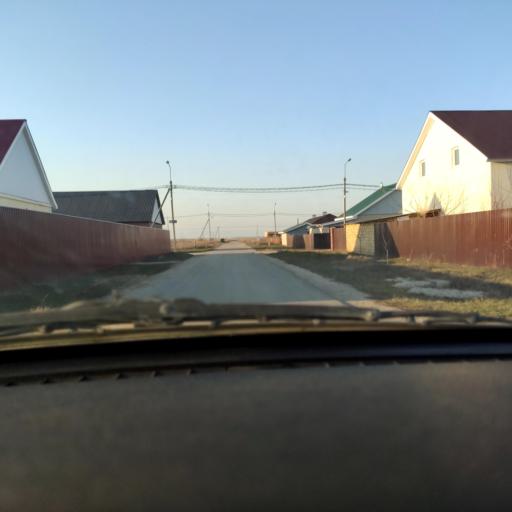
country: RU
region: Samara
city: Podstepki
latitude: 53.5753
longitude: 49.1135
